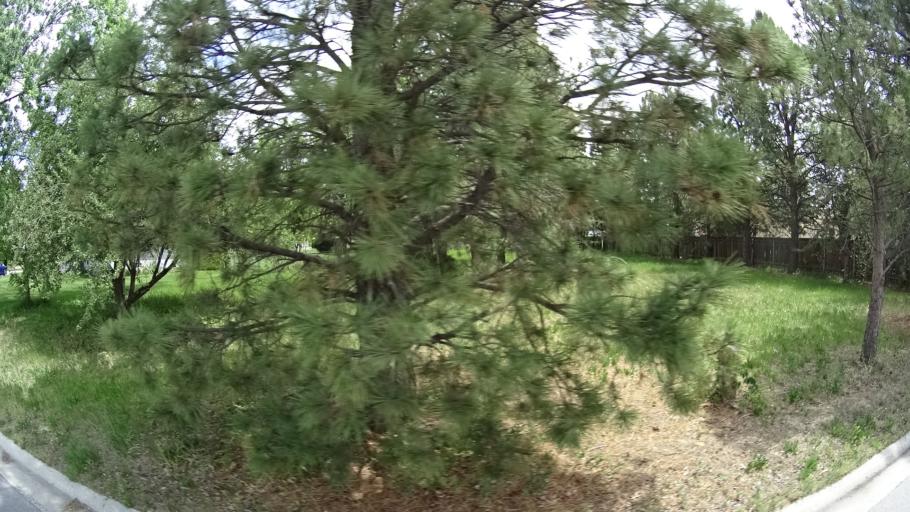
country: US
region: Idaho
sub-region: Ada County
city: Meridian
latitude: 43.6203
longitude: -116.3419
